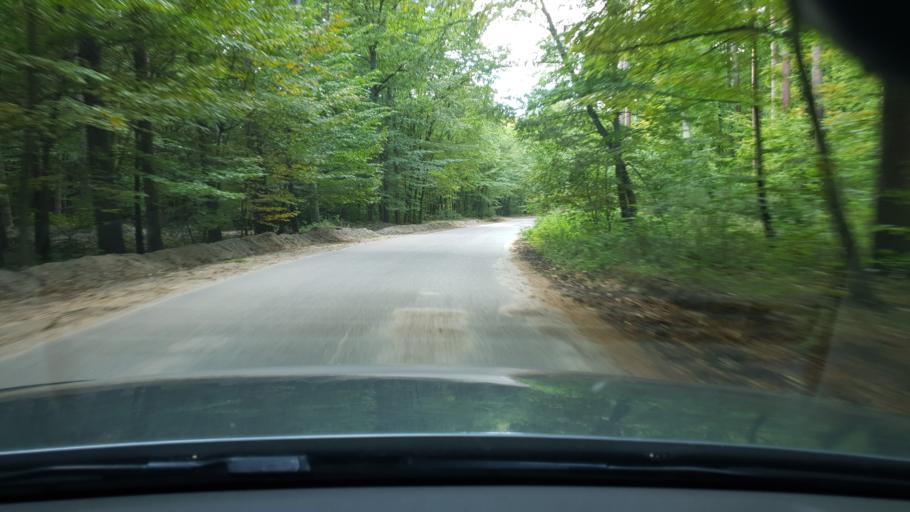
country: PL
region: Pomeranian Voivodeship
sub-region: Powiat wejherowski
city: Reda
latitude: 54.5893
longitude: 18.3341
